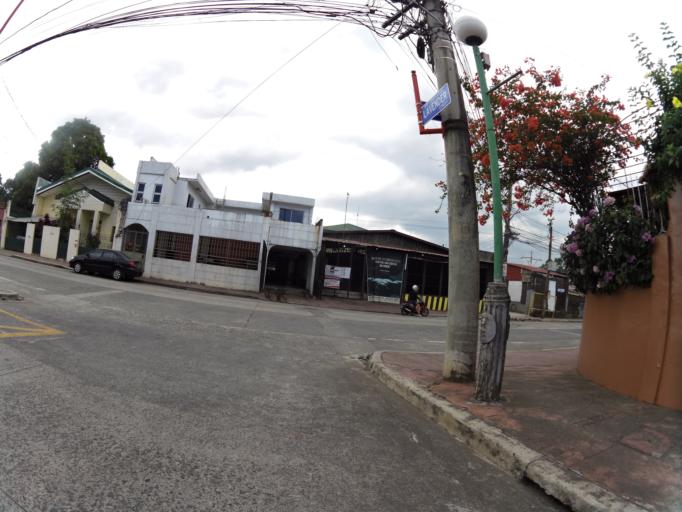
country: PH
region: Calabarzon
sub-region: Province of Rizal
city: Antipolo
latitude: 14.6387
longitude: 121.1141
